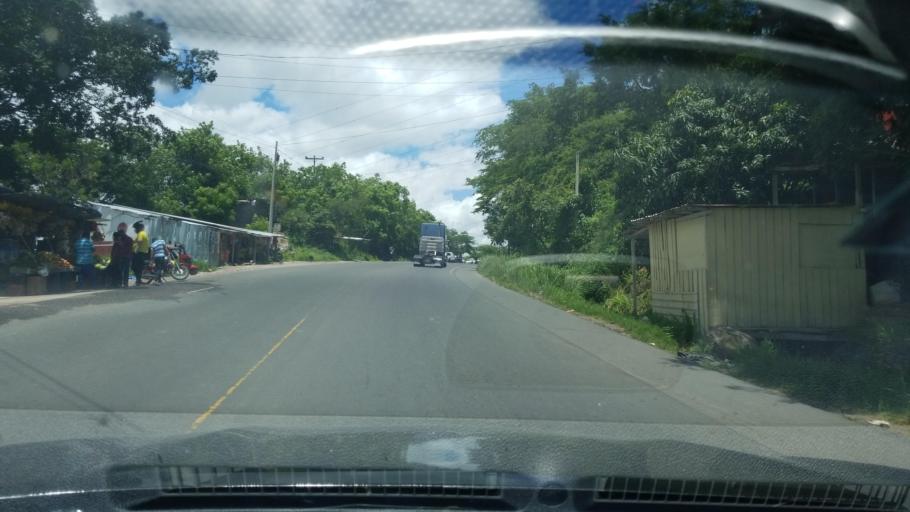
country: HN
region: Francisco Morazan
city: Rio Abajo
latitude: 14.1476
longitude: -87.2143
